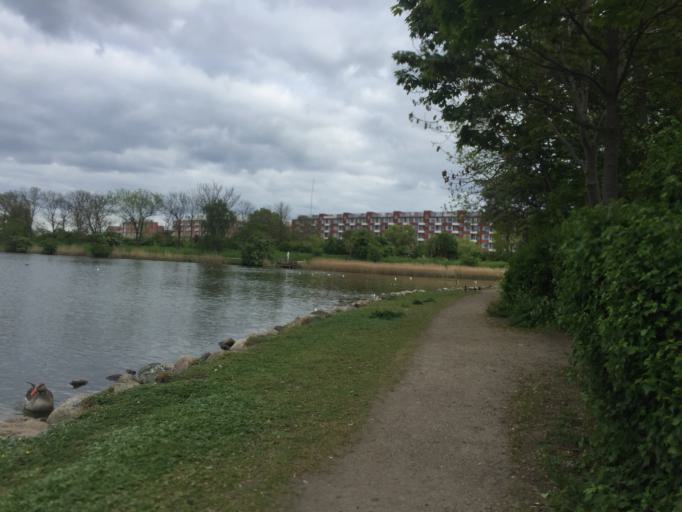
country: DK
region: Capital Region
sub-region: Kobenhavn
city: Christianshavn
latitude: 55.6705
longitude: 12.5959
